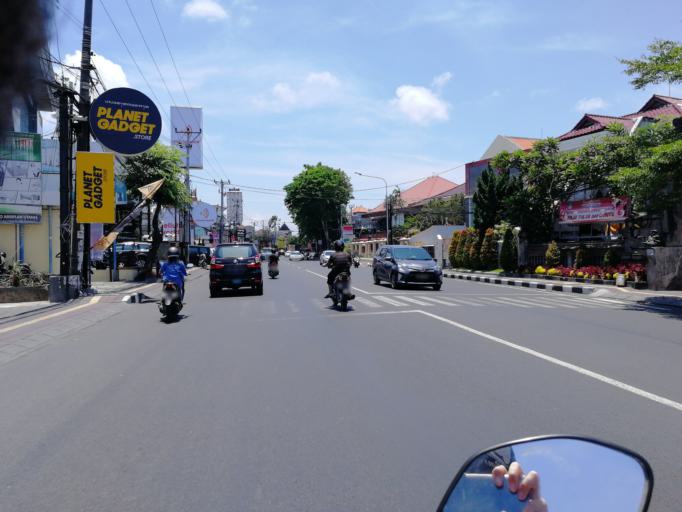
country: ID
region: Bali
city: Denpasar
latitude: -8.6714
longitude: 115.2092
